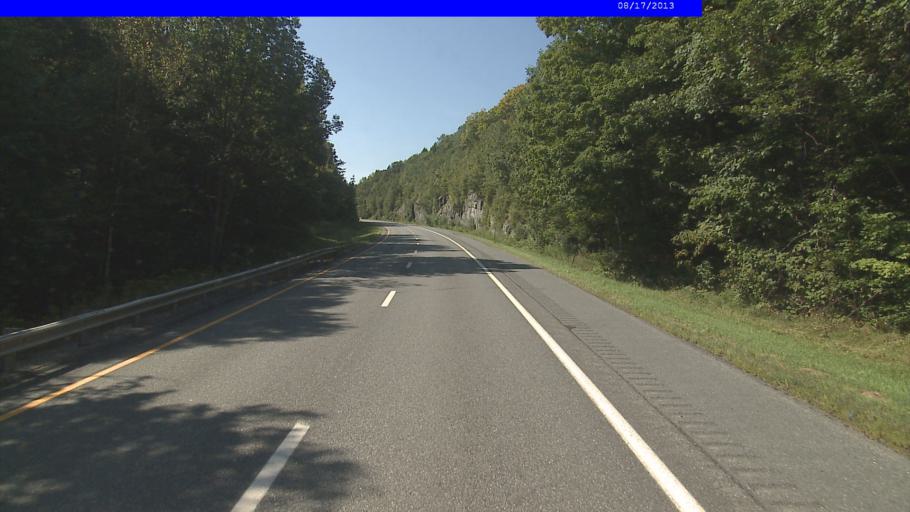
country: US
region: New Hampshire
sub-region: Sullivan County
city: Charlestown
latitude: 43.2465
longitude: -72.4482
